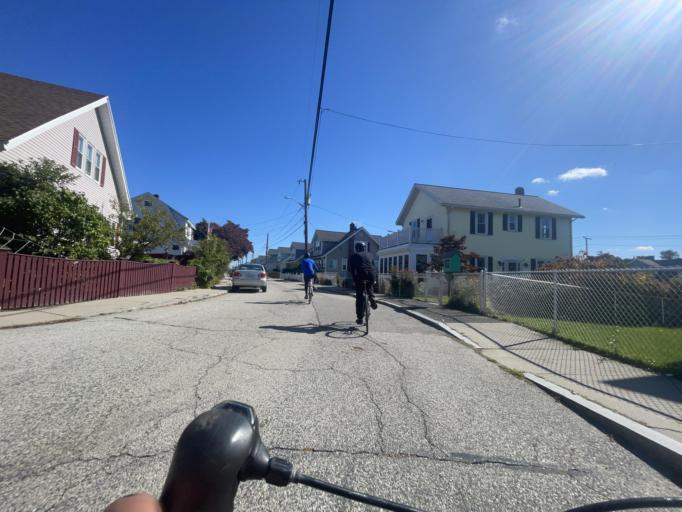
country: US
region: Massachusetts
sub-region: Norfolk County
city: Quincy
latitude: 42.2810
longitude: -71.0228
